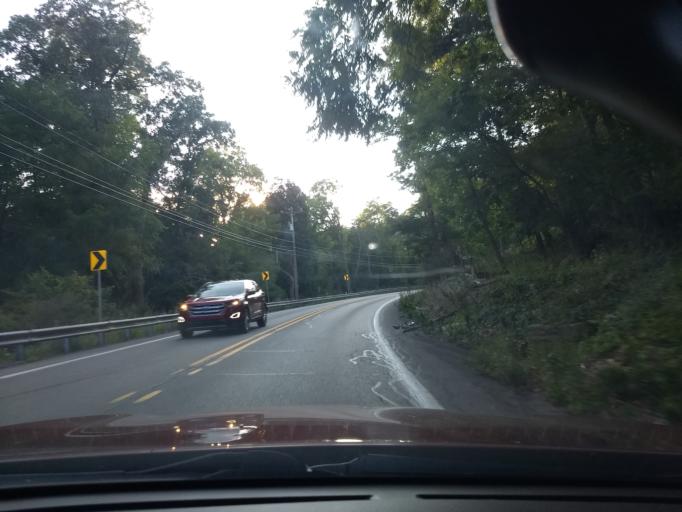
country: US
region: Pennsylvania
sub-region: Allegheny County
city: Gibsonia
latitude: 40.6312
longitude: -79.9986
